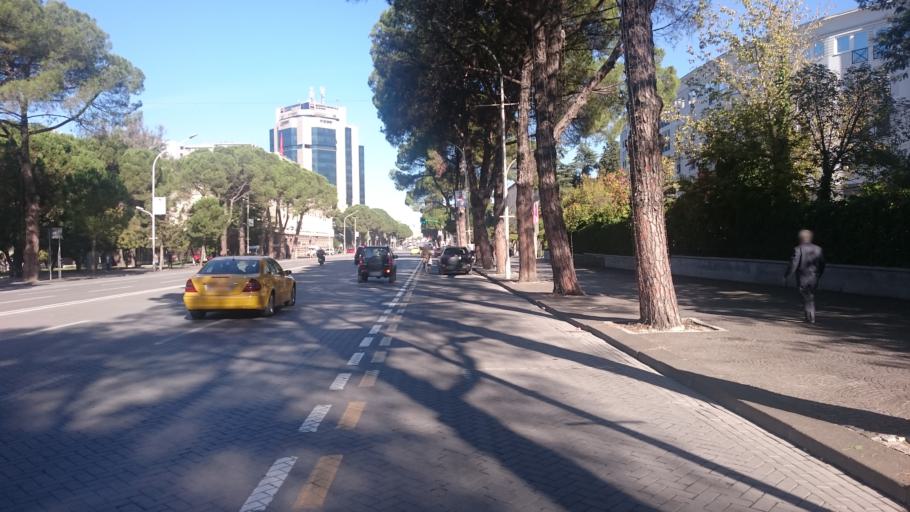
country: AL
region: Tirane
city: Tirana
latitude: 41.3200
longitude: 19.8208
